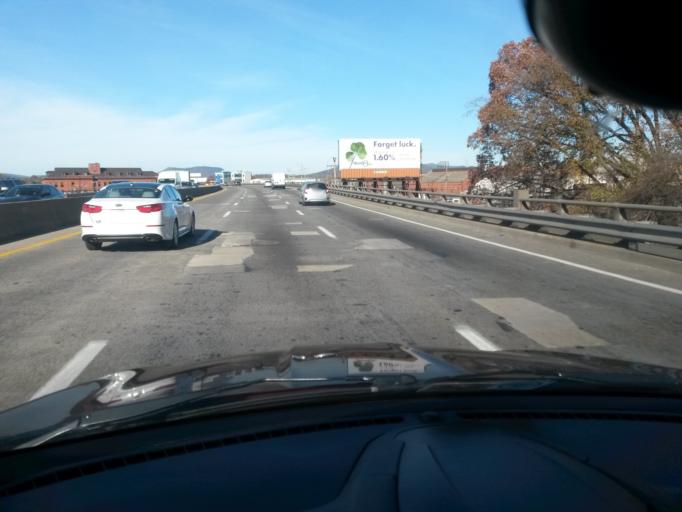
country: US
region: Virginia
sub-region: City of Roanoke
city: Roanoke
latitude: 37.2713
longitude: -79.9361
